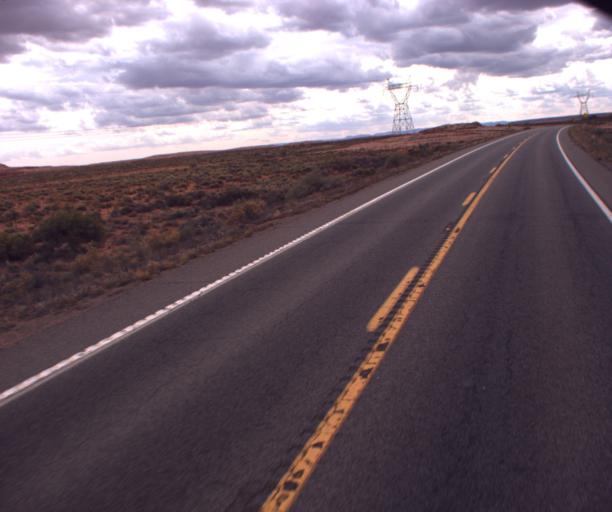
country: US
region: Arizona
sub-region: Navajo County
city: Kayenta
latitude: 36.8511
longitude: -109.8318
